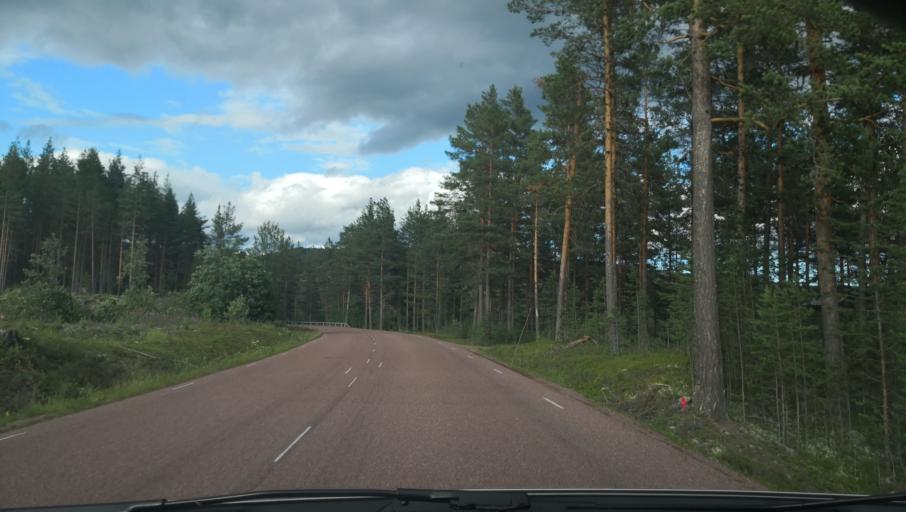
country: SE
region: Dalarna
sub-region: Alvdalens Kommun
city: AElvdalen
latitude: 61.3083
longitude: 13.7256
